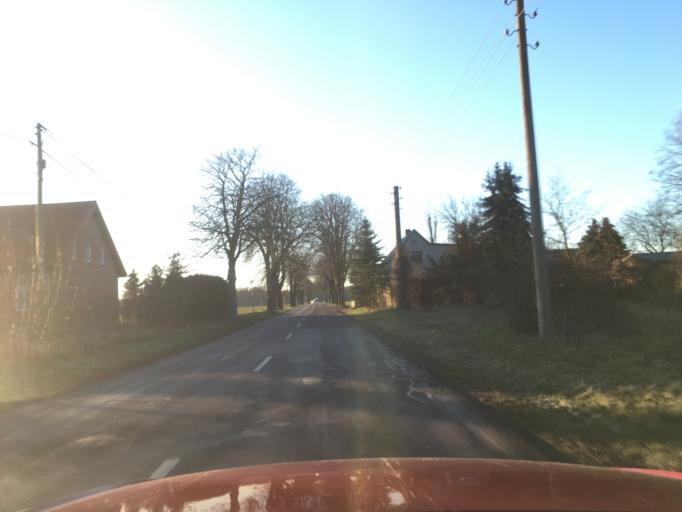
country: DE
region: Saxony-Anhalt
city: Klieken
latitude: 51.9243
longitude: 12.3156
